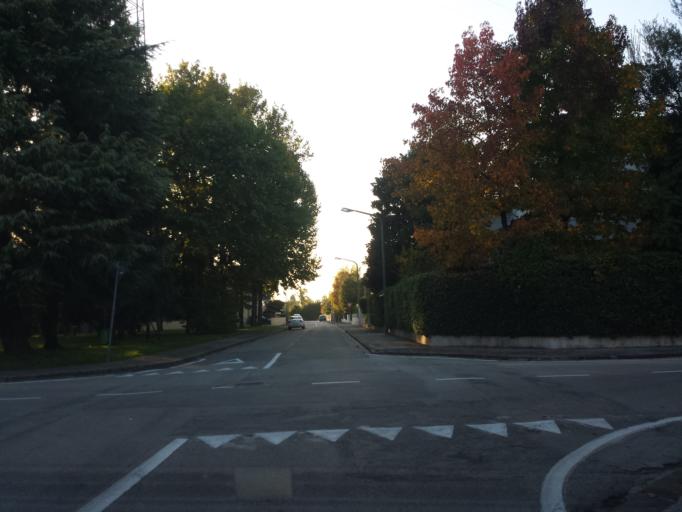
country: IT
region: Veneto
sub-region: Provincia di Vicenza
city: Vicenza
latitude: 45.5768
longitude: 11.5430
